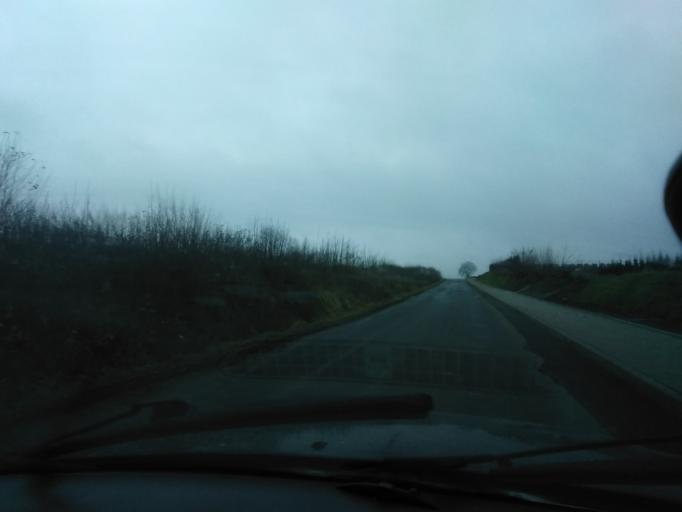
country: PL
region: Subcarpathian Voivodeship
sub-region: Powiat jaroslawski
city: Rokietnica
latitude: 49.9137
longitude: 22.6120
